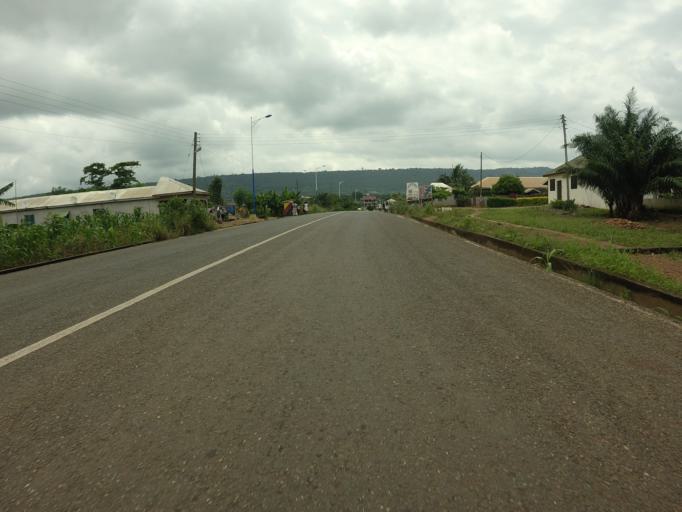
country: GH
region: Volta
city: Ho
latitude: 6.6255
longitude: 0.4902
